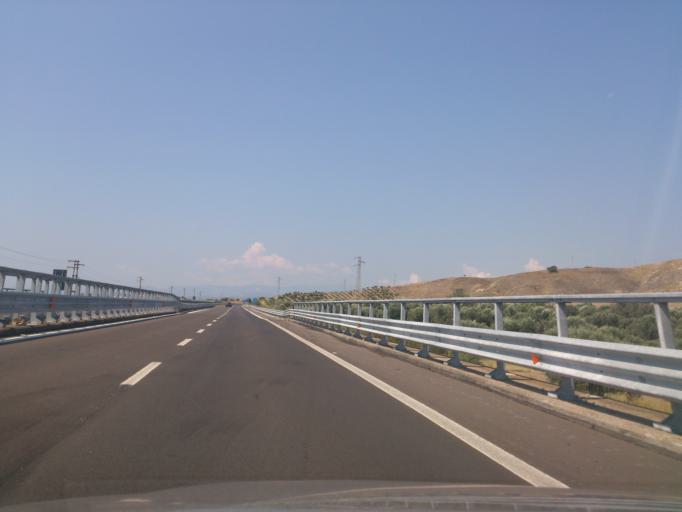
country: IT
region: Calabria
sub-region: Provincia di Reggio Calabria
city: Roccella Ionica
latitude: 38.3146
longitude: 16.3686
